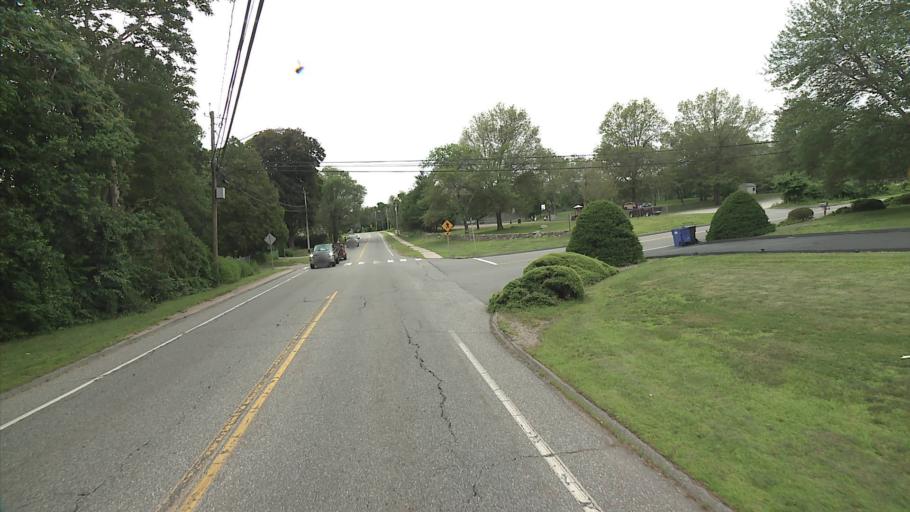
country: US
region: Connecticut
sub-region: New London County
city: Long Hill
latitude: 41.3866
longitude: -72.0274
